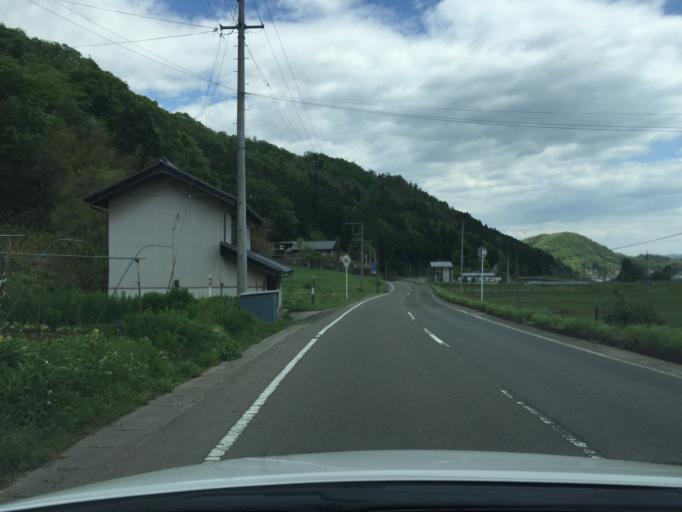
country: JP
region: Fukushima
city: Hobaramachi
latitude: 37.7561
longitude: 140.5691
